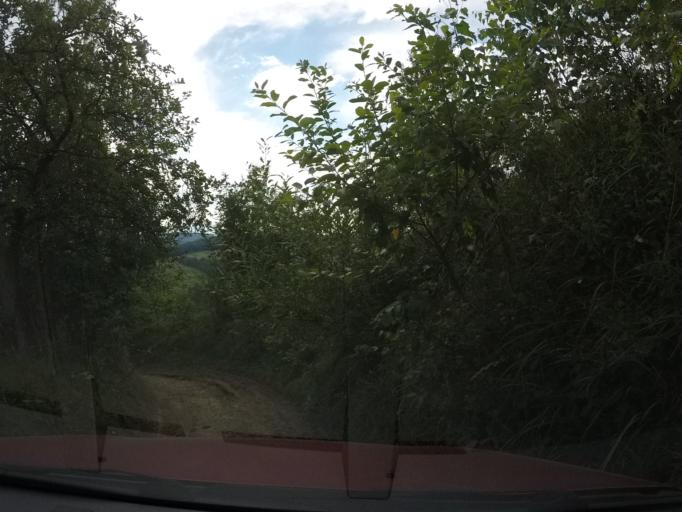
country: UA
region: Zakarpattia
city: Velykyi Bereznyi
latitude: 49.0306
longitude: 22.5906
